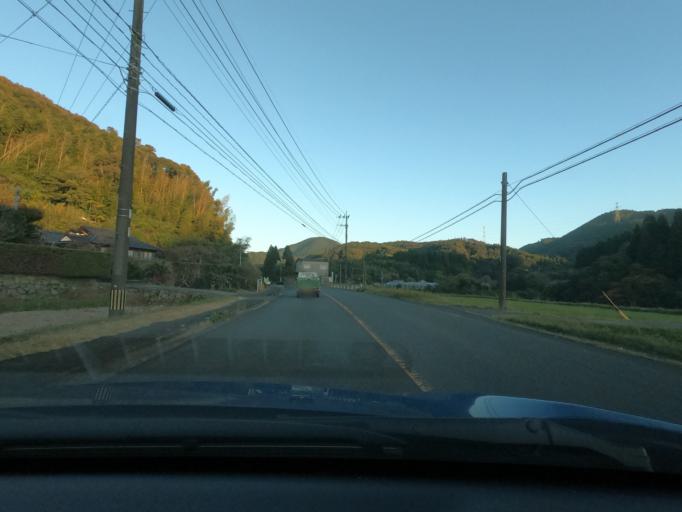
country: JP
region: Kagoshima
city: Satsumasendai
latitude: 31.7901
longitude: 130.4652
